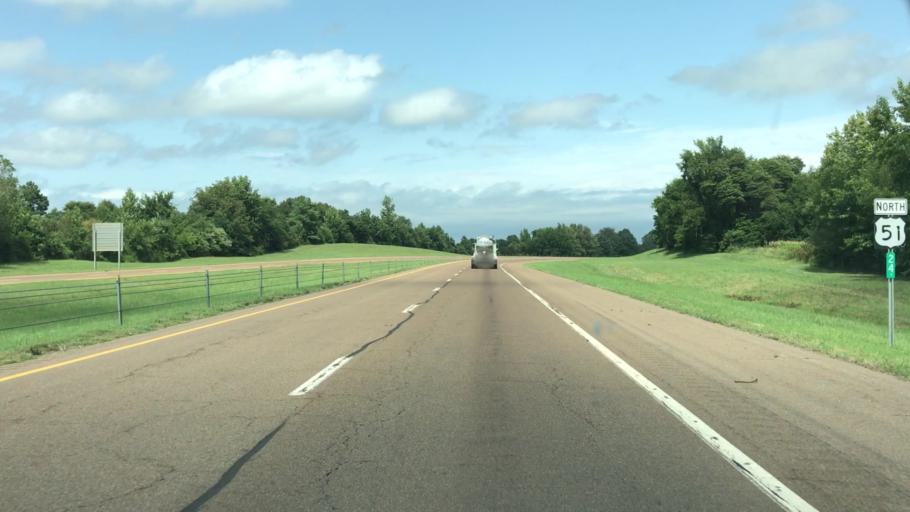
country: US
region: Tennessee
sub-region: Obion County
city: Union City
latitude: 36.4554
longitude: -88.9982
